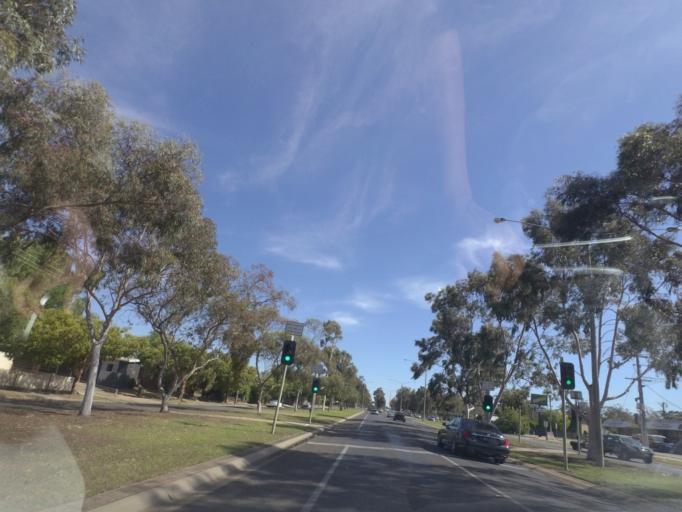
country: AU
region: Victoria
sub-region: Greater Shepparton
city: Shepparton
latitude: -36.4001
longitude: 145.3955
